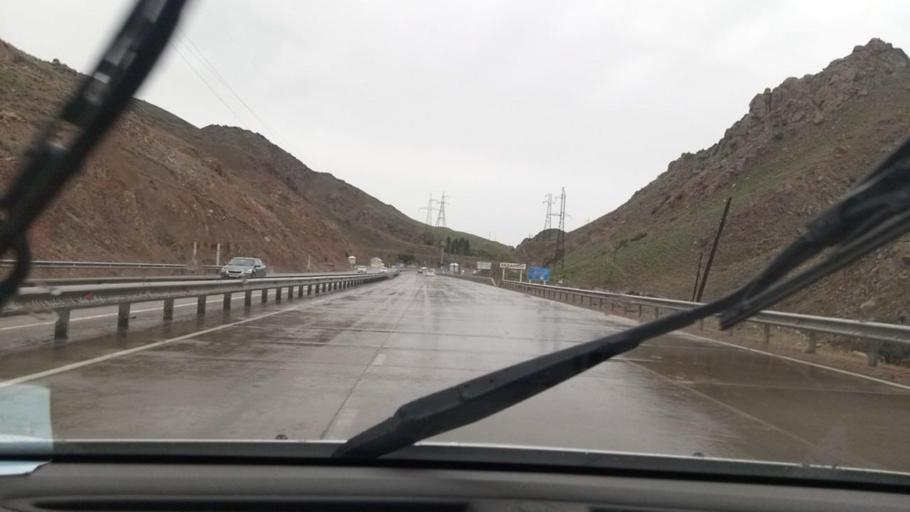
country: TJ
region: Viloyati Sughd
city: Shaydon
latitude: 40.9619
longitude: 70.6628
